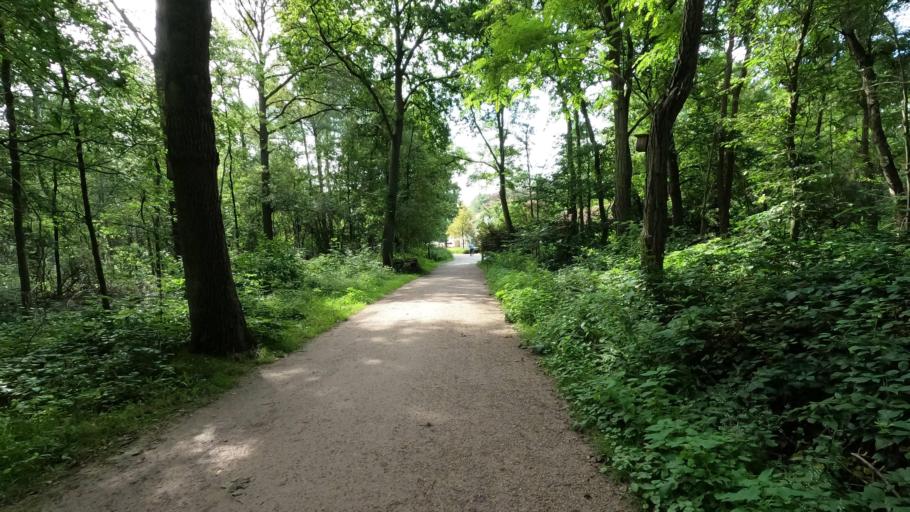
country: BE
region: Flanders
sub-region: Provincie Antwerpen
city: Heist-op-den-Berg
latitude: 51.0906
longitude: 4.7080
